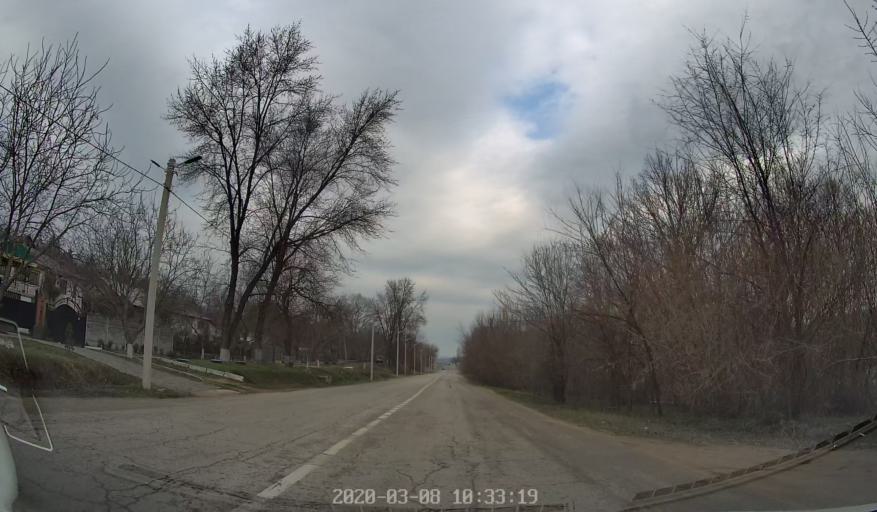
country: MD
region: Orhei
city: Orhei
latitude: 47.3994
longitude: 28.8197
